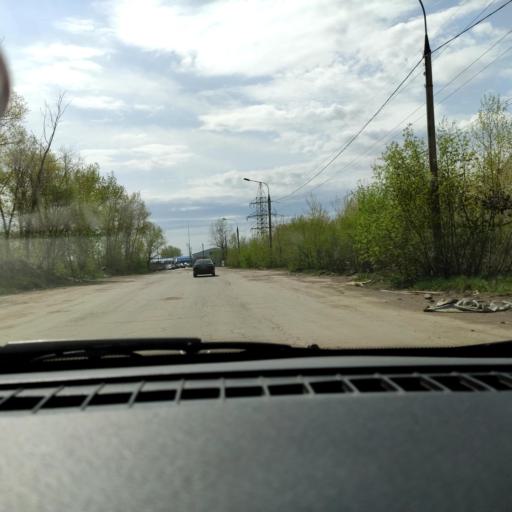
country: RU
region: Samara
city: Samara
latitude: 53.1775
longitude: 50.1241
